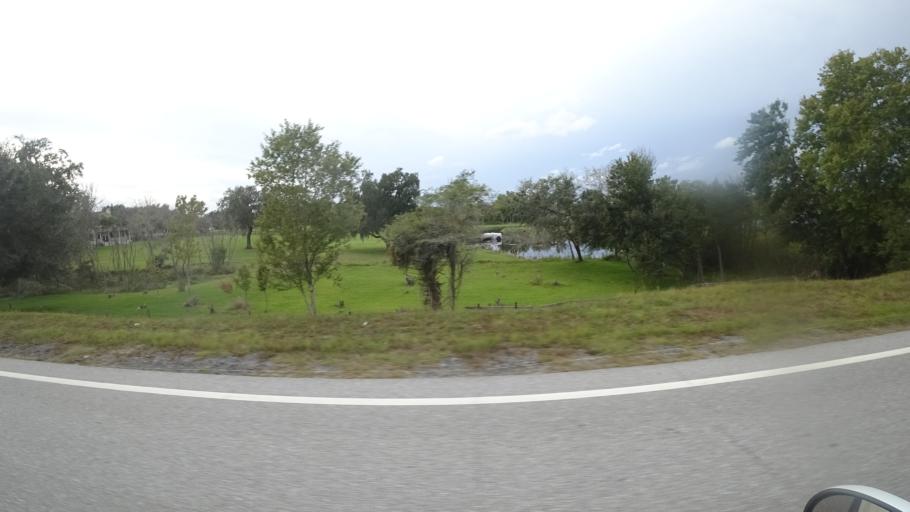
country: US
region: Florida
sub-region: Sarasota County
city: The Meadows
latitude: 27.4659
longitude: -82.2704
